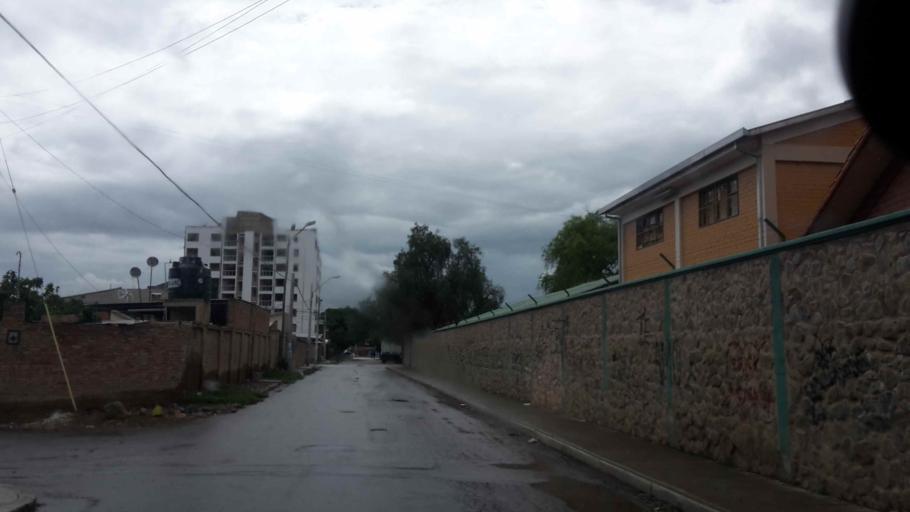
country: BO
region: Cochabamba
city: Cochabamba
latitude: -17.3983
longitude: -66.1837
